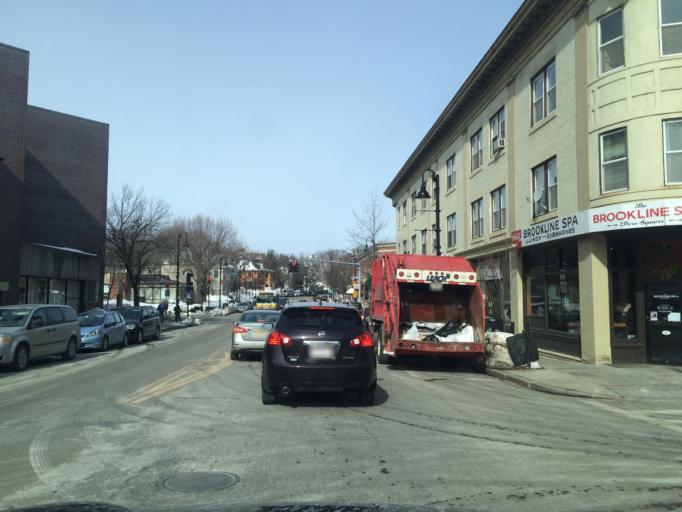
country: US
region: Massachusetts
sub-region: Norfolk County
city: Brookline
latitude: 42.3355
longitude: -71.1200
